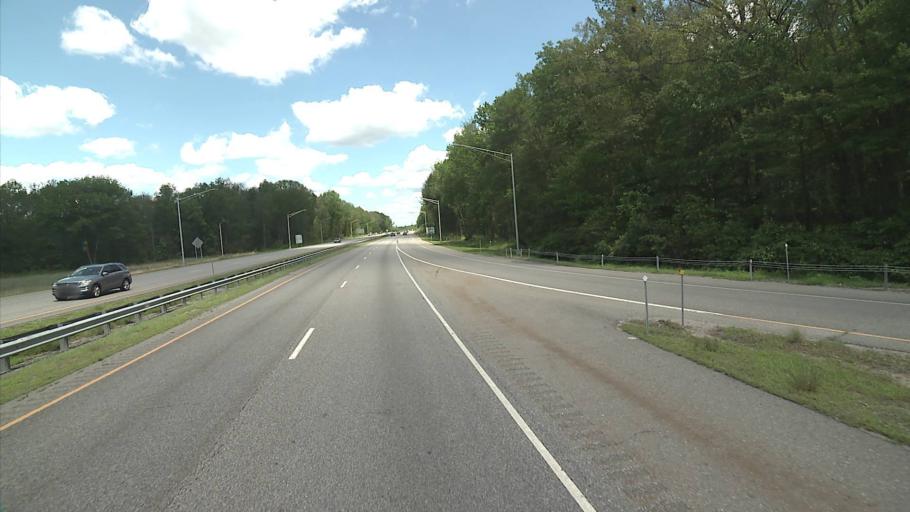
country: US
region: Connecticut
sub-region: Windham County
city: Moosup
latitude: 41.7205
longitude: -71.8938
